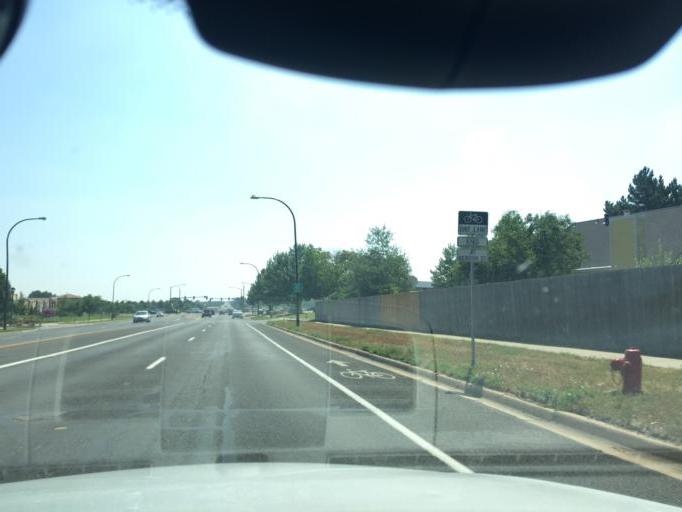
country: US
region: Colorado
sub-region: Broomfield County
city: Broomfield
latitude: 39.8997
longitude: -105.0560
